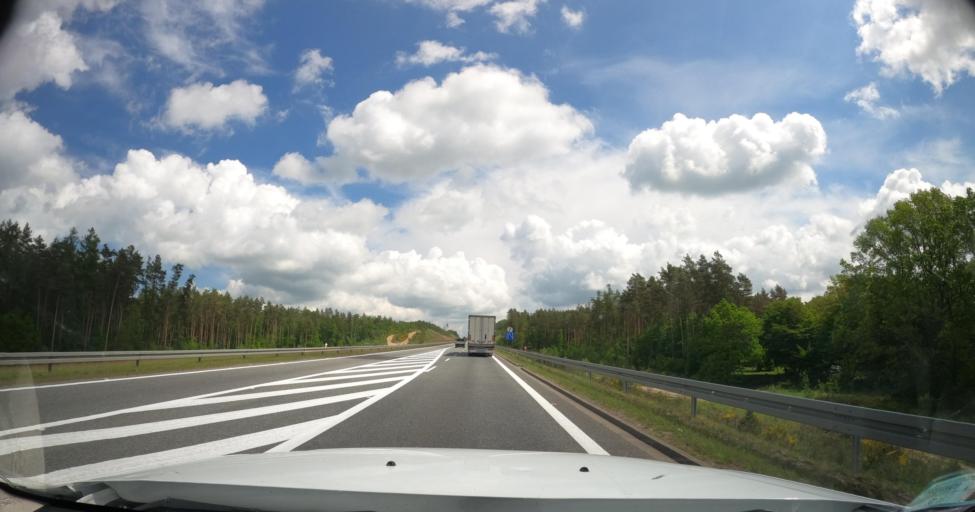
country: PL
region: Pomeranian Voivodeship
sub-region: Powiat slupski
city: Kobylnica
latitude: 54.4274
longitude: 17.0310
